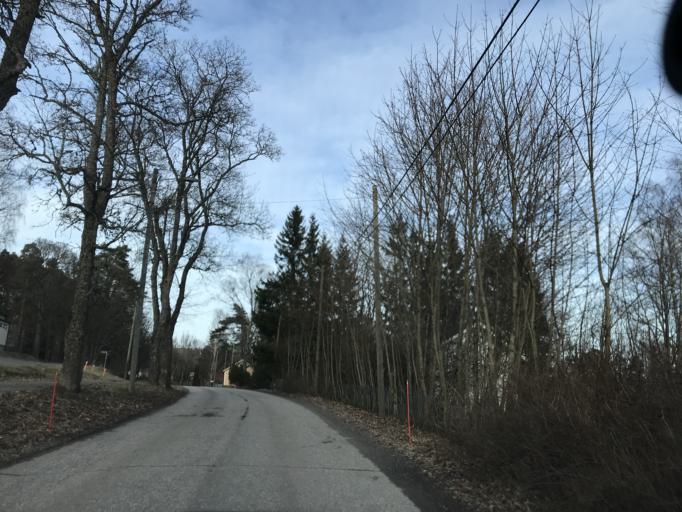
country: FI
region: Uusimaa
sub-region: Raaseporin
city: Pohja
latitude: 60.0931
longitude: 23.5187
